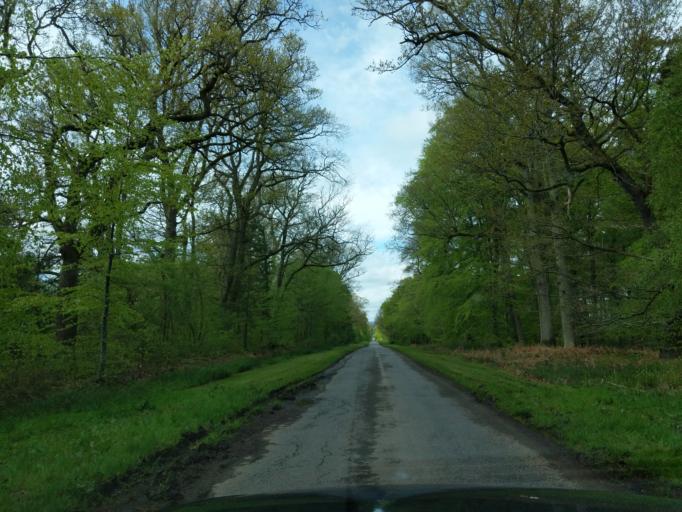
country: GB
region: Scotland
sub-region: The Scottish Borders
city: Saint Boswells
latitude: 55.6425
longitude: -2.5729
